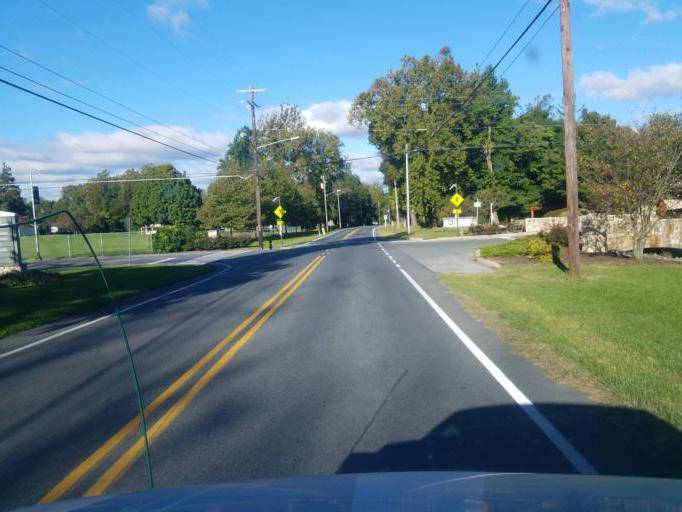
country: US
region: Pennsylvania
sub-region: Franklin County
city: Mont Alto
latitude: 39.8400
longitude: -77.5438
